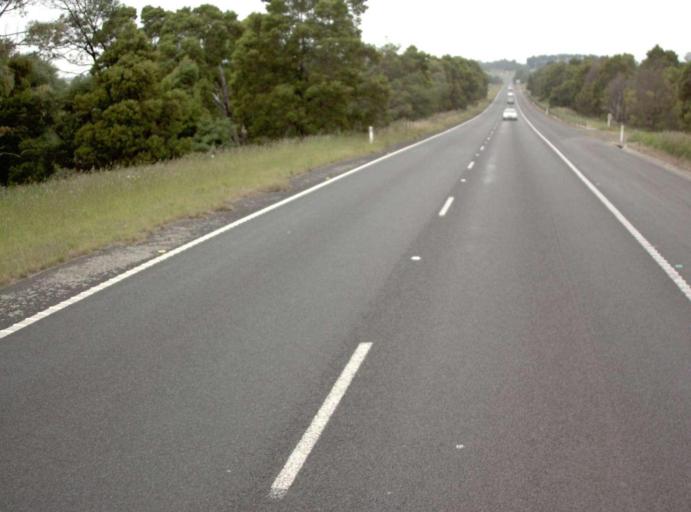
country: AU
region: Victoria
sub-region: Baw Baw
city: Warragul
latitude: -38.1764
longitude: 145.9774
